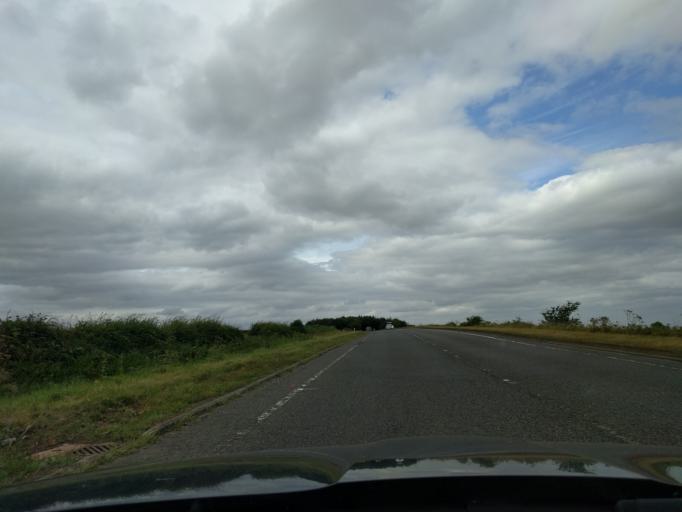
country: GB
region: England
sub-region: Northumberland
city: Ellingham
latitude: 55.5255
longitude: -1.7547
